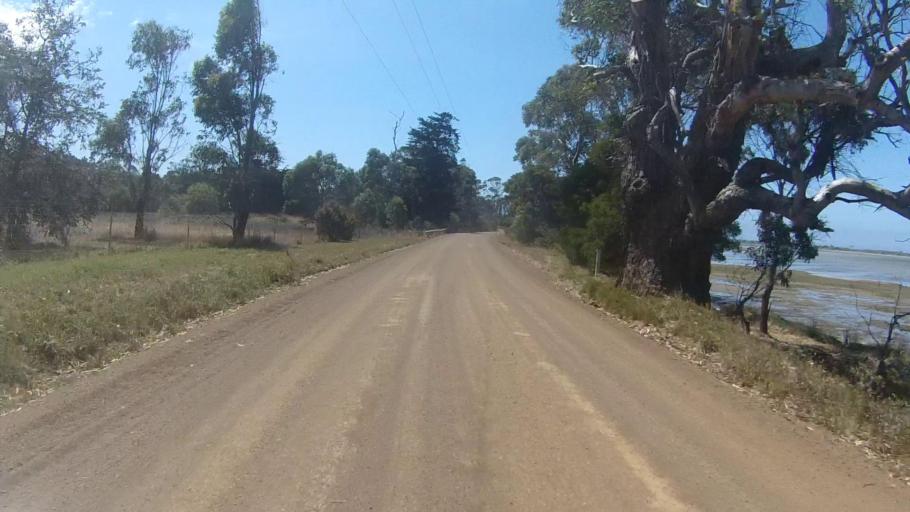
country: AU
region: Tasmania
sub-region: Sorell
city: Sorell
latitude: -42.8381
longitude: 147.8531
